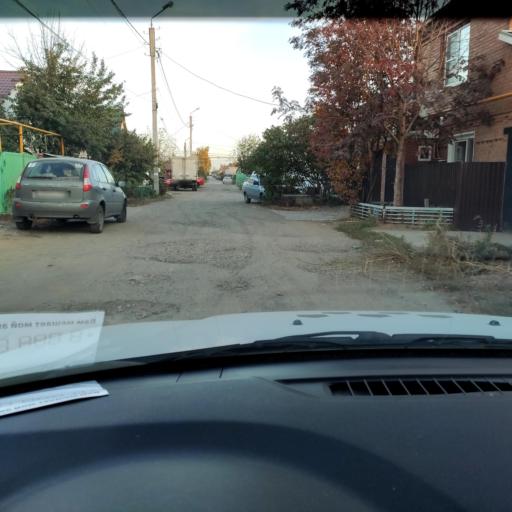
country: RU
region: Samara
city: Tol'yatti
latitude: 53.5358
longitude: 49.4250
